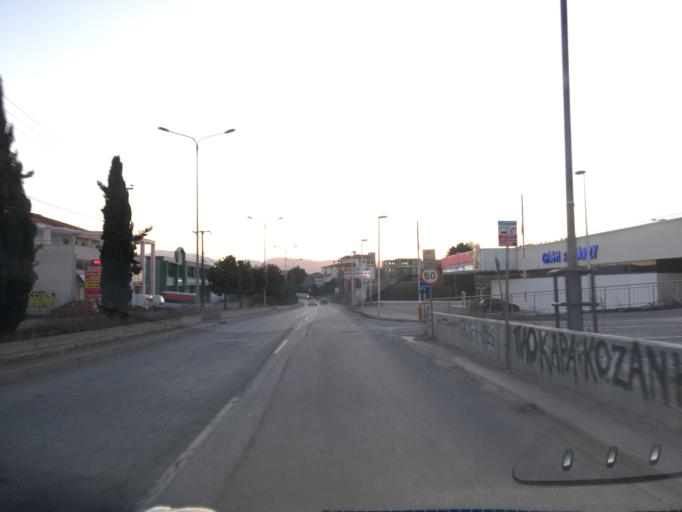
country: GR
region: West Macedonia
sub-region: Nomos Kozanis
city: Kozani
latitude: 40.3056
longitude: 21.8079
